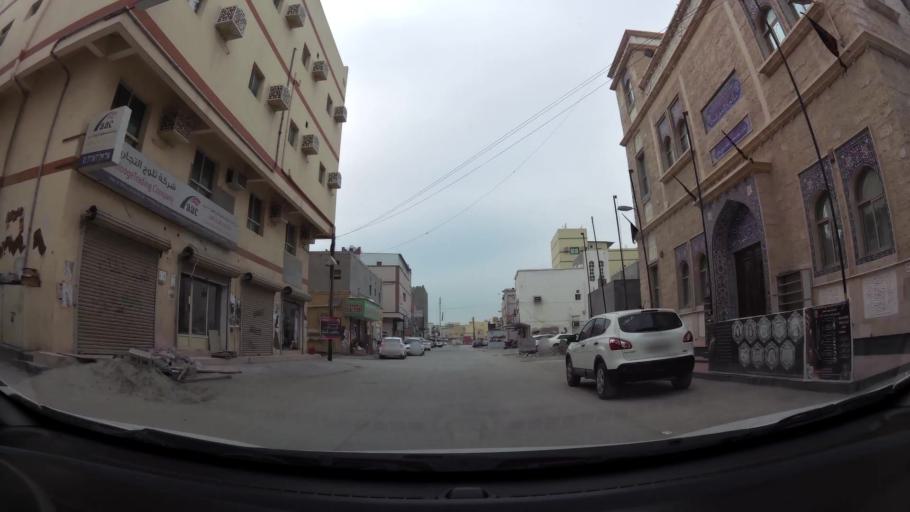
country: BH
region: Northern
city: Sitrah
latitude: 26.1345
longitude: 50.6130
